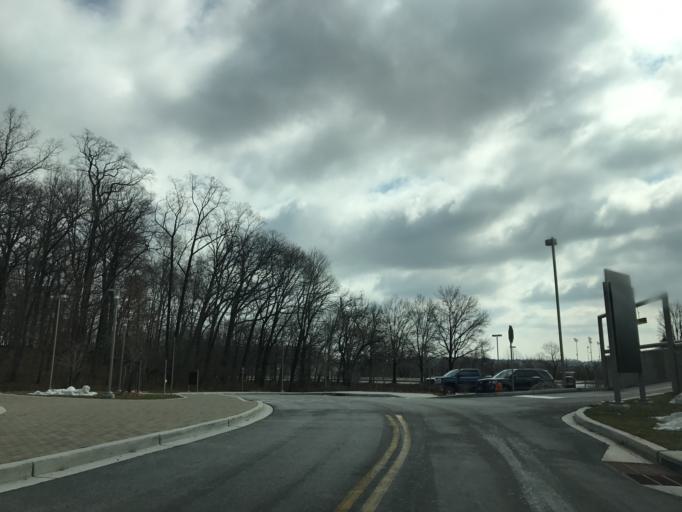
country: US
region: Maryland
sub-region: Baltimore County
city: Arbutus
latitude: 39.2520
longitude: -76.7121
